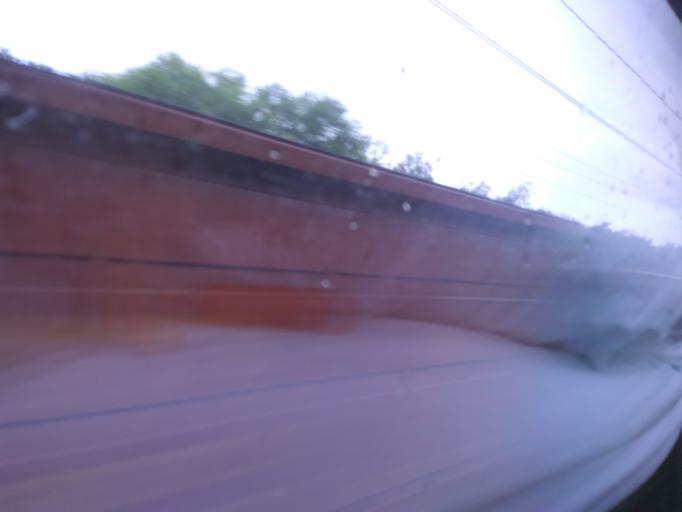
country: RU
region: Moskovskaya
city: Ozery
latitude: 54.7143
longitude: 38.4469
